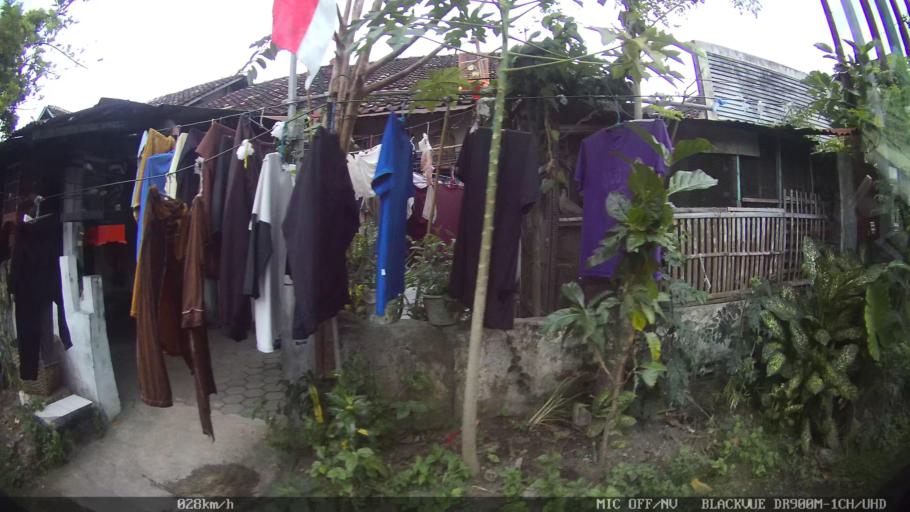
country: ID
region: Daerah Istimewa Yogyakarta
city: Depok
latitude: -7.8192
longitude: 110.4158
